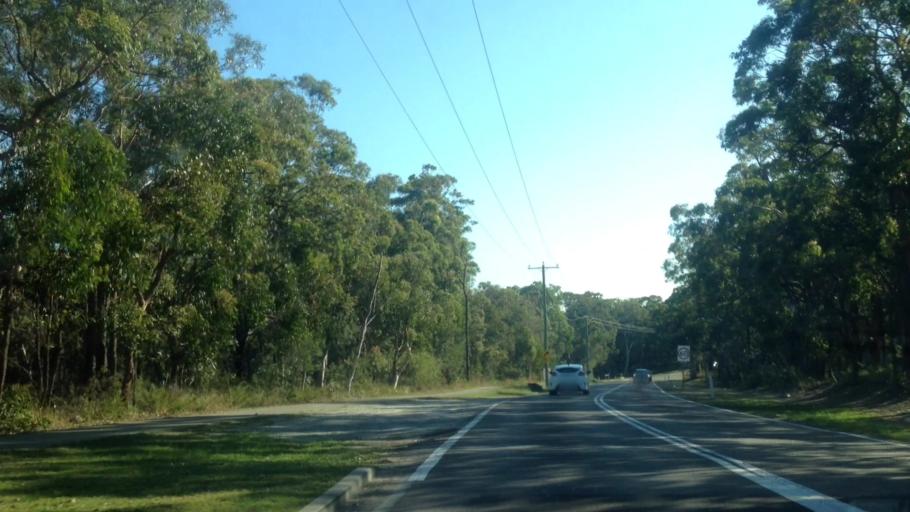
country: AU
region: New South Wales
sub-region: Lake Macquarie Shire
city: Dora Creek
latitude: -33.1115
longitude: 151.5306
